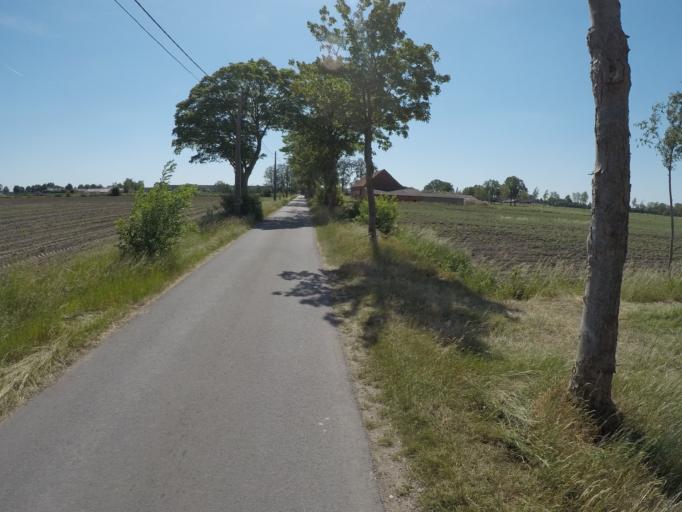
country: BE
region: Flanders
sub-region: Provincie Antwerpen
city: Wuustwezel
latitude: 51.4248
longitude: 4.6146
